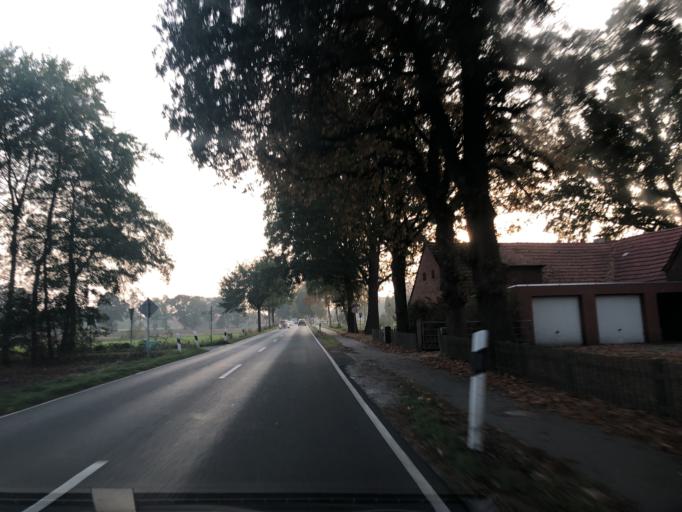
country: DE
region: Lower Saxony
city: Wardenburg
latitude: 53.0870
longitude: 8.1775
